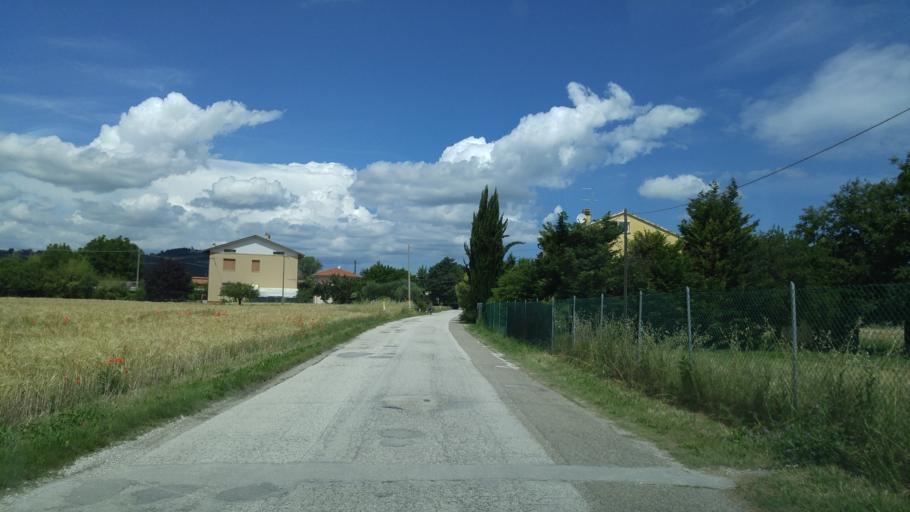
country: IT
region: The Marches
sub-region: Provincia di Pesaro e Urbino
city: Bellocchi
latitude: 43.8009
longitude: 13.0091
